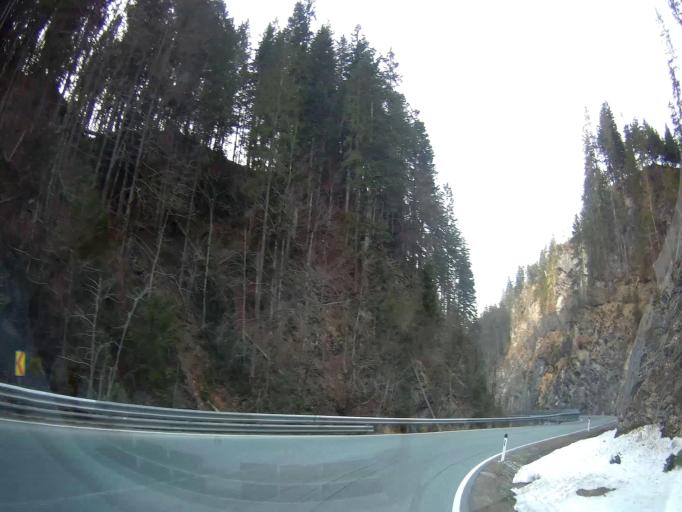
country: AT
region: Salzburg
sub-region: Politischer Bezirk Hallein
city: Abtenau
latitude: 47.5425
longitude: 13.4209
